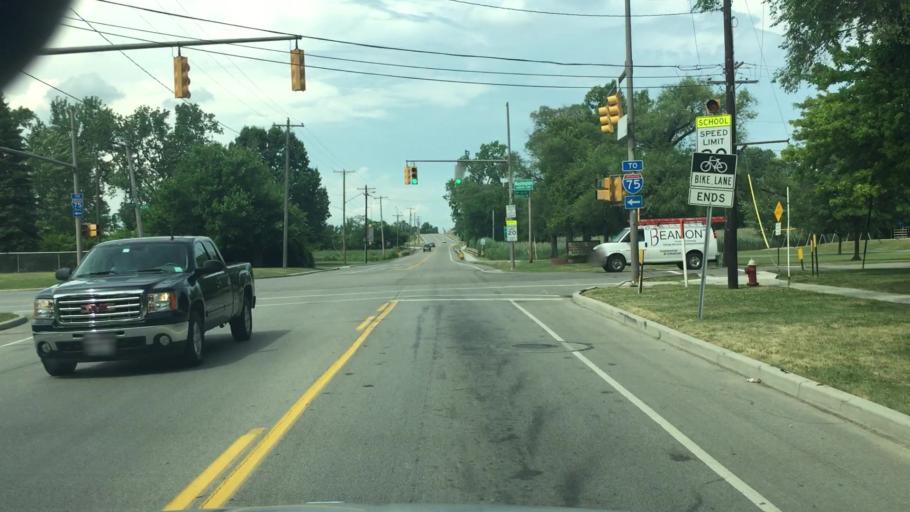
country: US
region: Ohio
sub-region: Lucas County
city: Oregon
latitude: 41.7197
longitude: -83.4971
